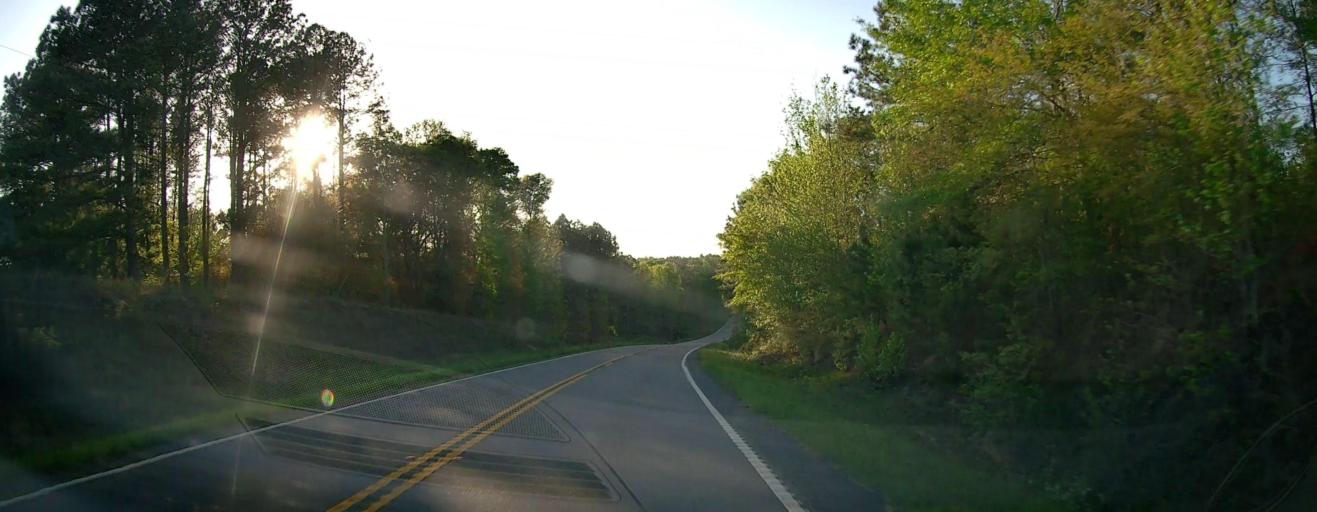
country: US
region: Georgia
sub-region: Schley County
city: Ellaville
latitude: 32.3460
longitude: -84.3717
